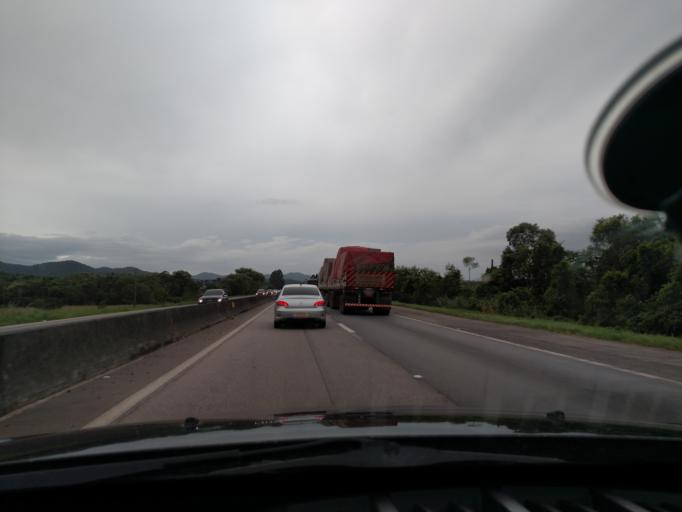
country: BR
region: Santa Catarina
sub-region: Biguacu
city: Biguacu
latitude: -27.4180
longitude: -48.6262
